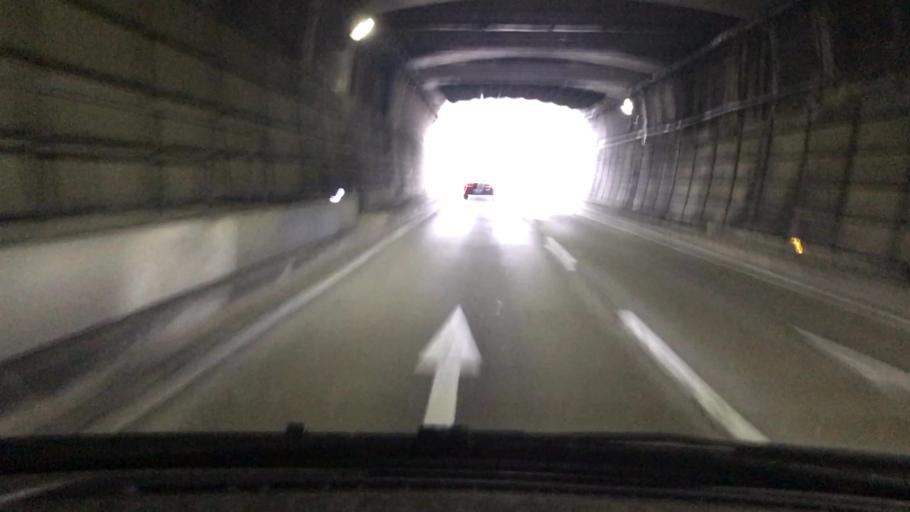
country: JP
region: Hyogo
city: Kobe
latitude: 34.7517
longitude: 135.1641
